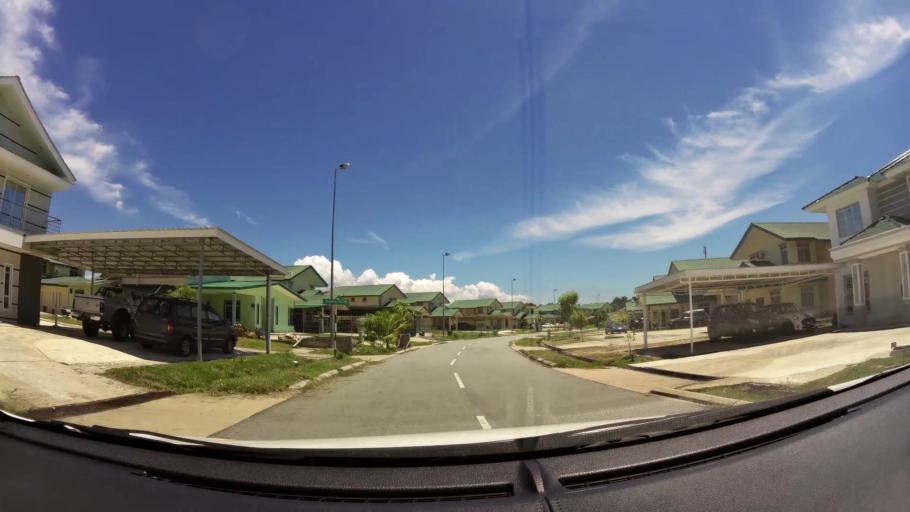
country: BN
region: Brunei and Muara
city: Bandar Seri Begawan
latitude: 5.0217
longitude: 115.0345
